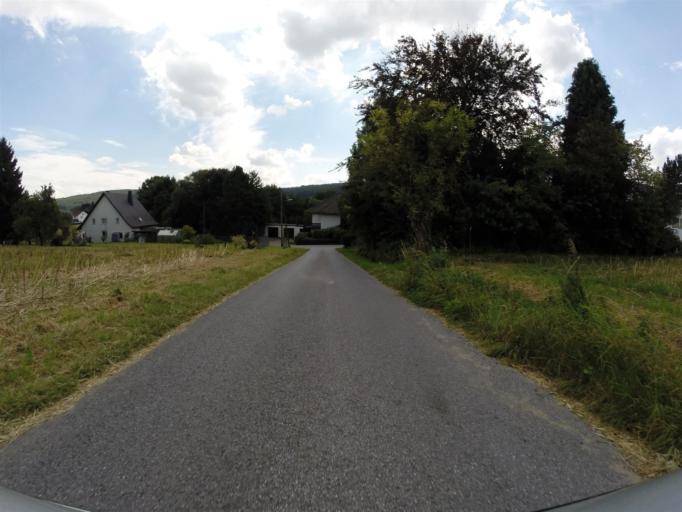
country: DE
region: North Rhine-Westphalia
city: Preussisch Oldendorf
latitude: 52.2759
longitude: 8.4998
